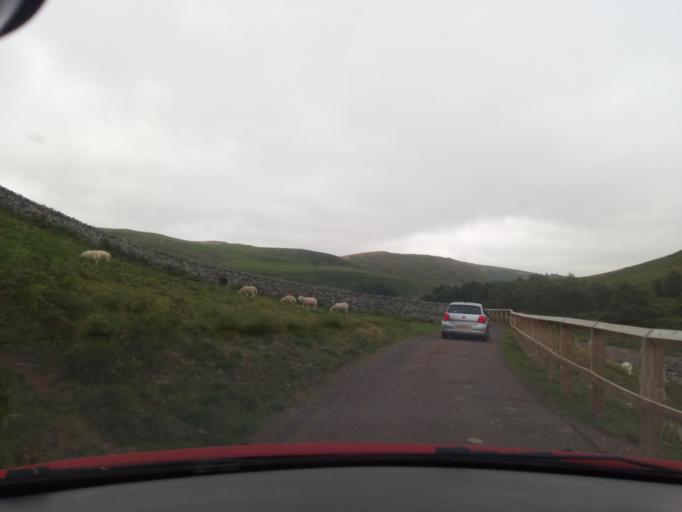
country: GB
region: England
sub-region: Northumberland
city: Rochester
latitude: 55.3645
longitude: -2.1906
